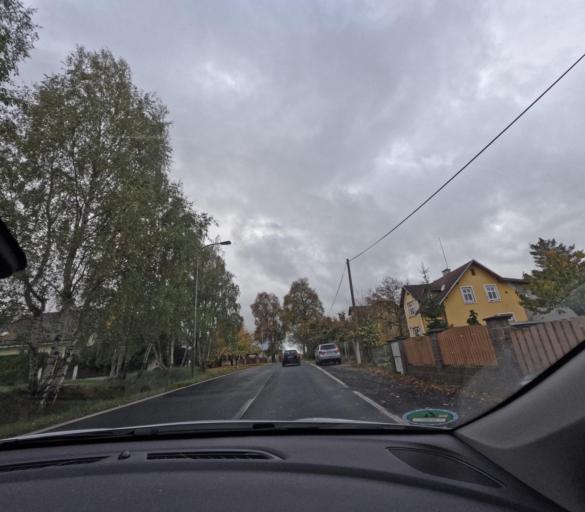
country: CZ
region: Karlovarsky
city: Dalovice
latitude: 50.2094
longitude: 12.9178
